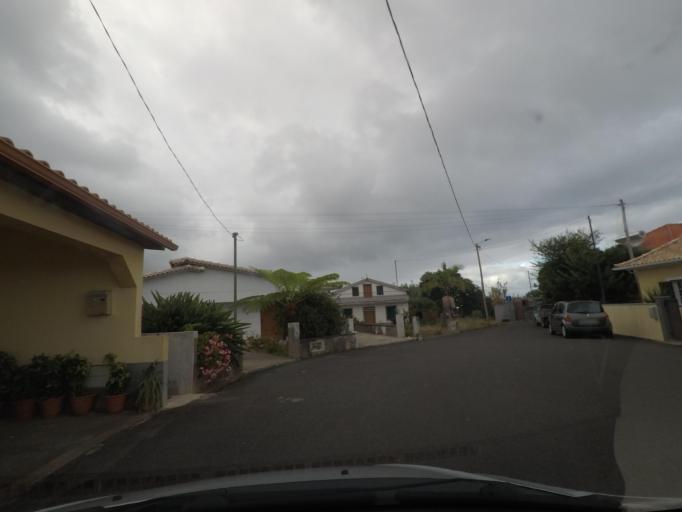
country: PT
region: Madeira
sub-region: Santana
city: Santana
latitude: 32.8157
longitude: -16.8791
